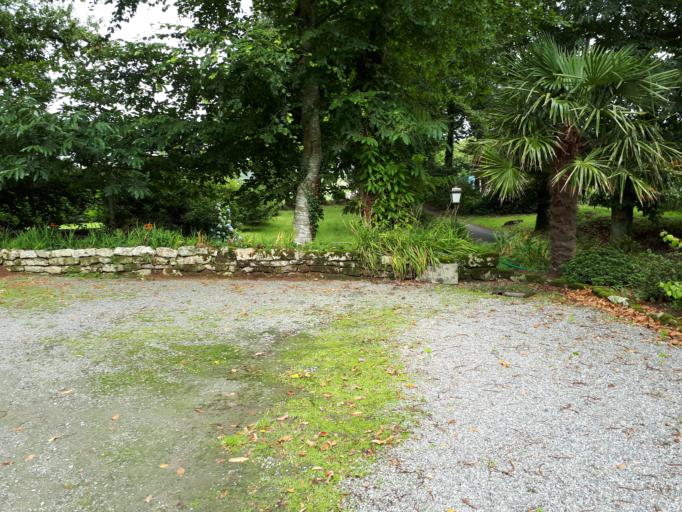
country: FR
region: Brittany
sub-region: Departement du Finistere
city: Plogastel-Saint-Germain
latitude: 47.9753
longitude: -4.2286
